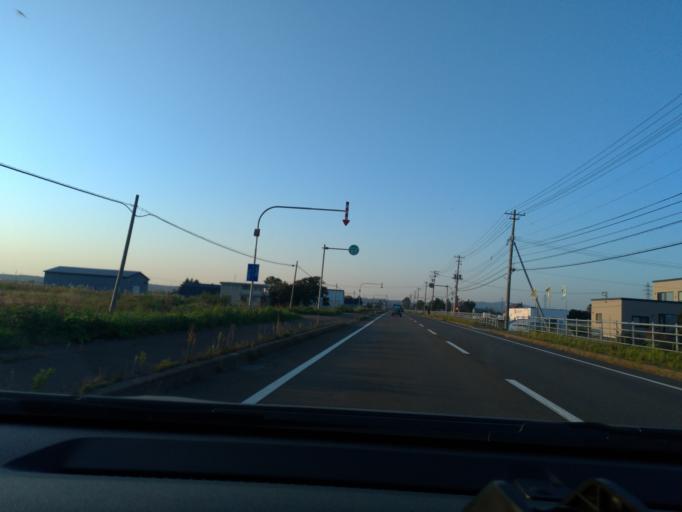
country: JP
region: Hokkaido
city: Tobetsu
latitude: 43.1942
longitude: 141.5239
